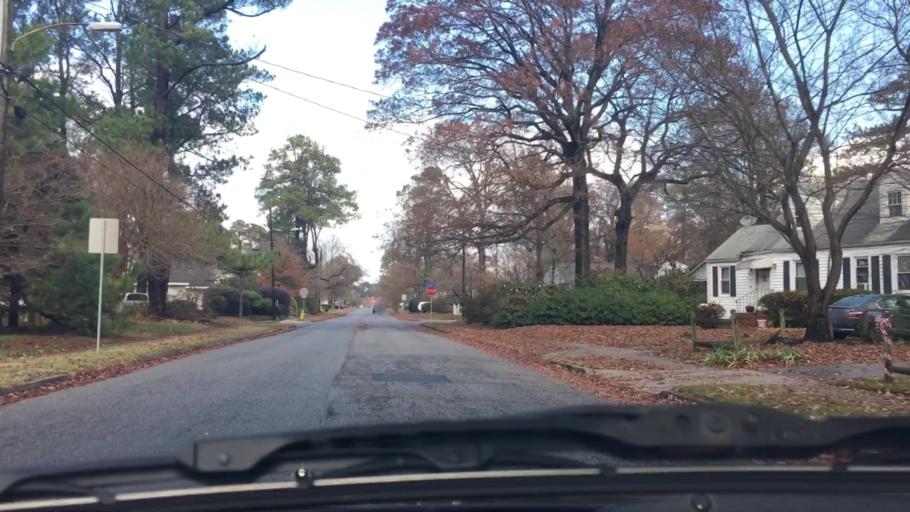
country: US
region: Virginia
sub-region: City of Norfolk
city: Norfolk
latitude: 36.9229
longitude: -76.2464
